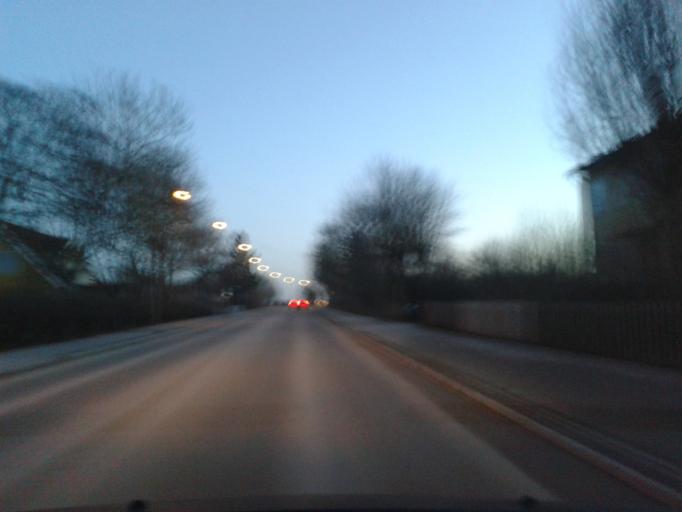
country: SE
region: Gotland
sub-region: Gotland
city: Visby
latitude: 57.6297
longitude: 18.3152
